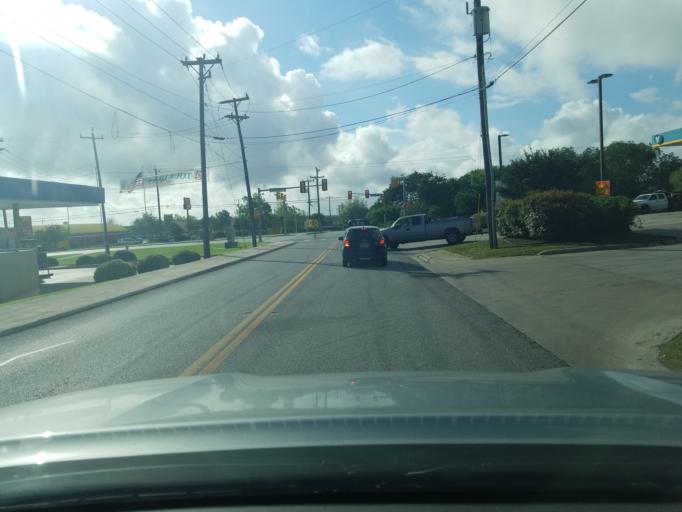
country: US
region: Texas
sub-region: Bexar County
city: Live Oak
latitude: 29.5902
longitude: -98.3565
